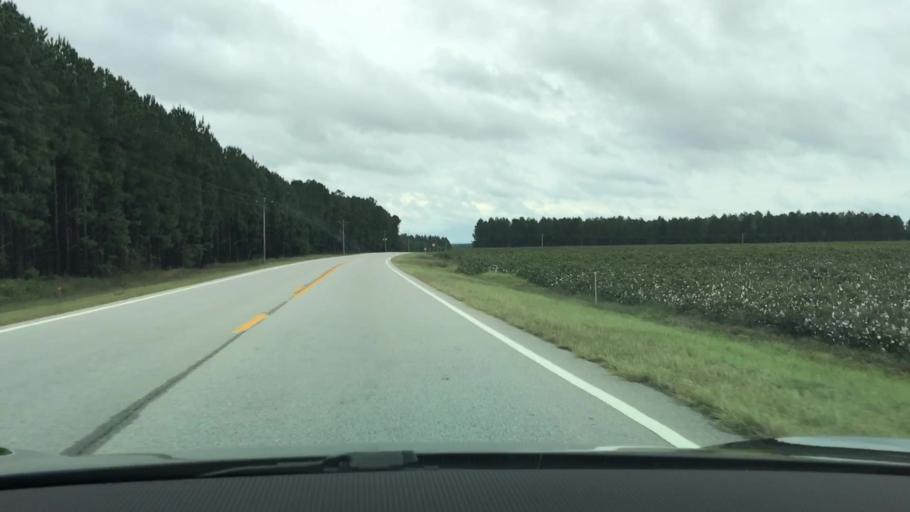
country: US
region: Georgia
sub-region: Glascock County
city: Gibson
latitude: 33.2866
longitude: -82.5070
